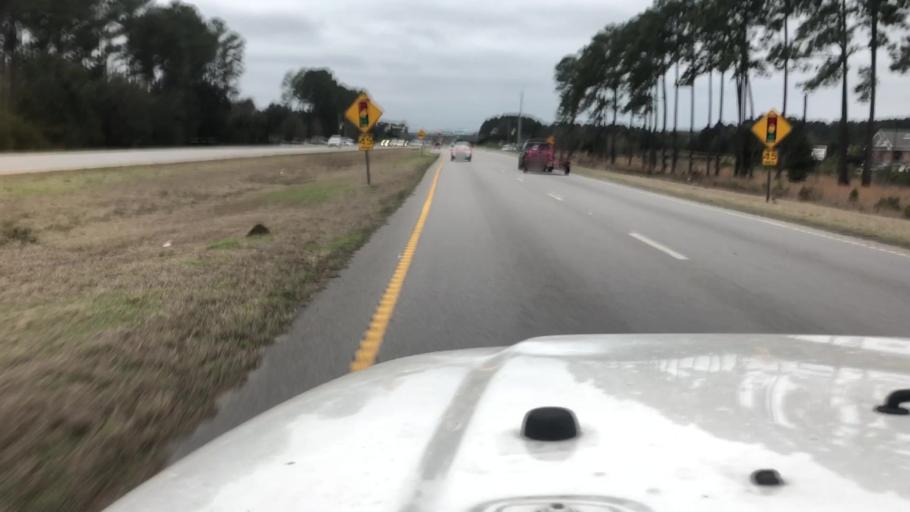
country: US
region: South Carolina
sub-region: Beaufort County
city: Bluffton
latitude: 32.2983
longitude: -80.9445
